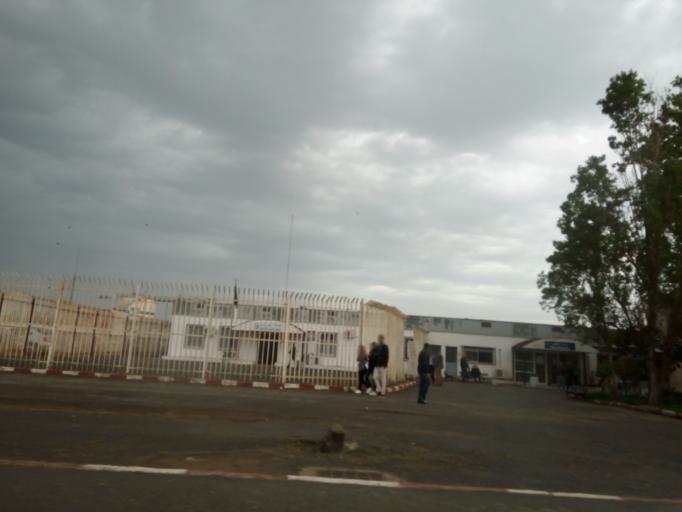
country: DZ
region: Alger
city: Dar el Beida
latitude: 36.7019
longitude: 3.2110
